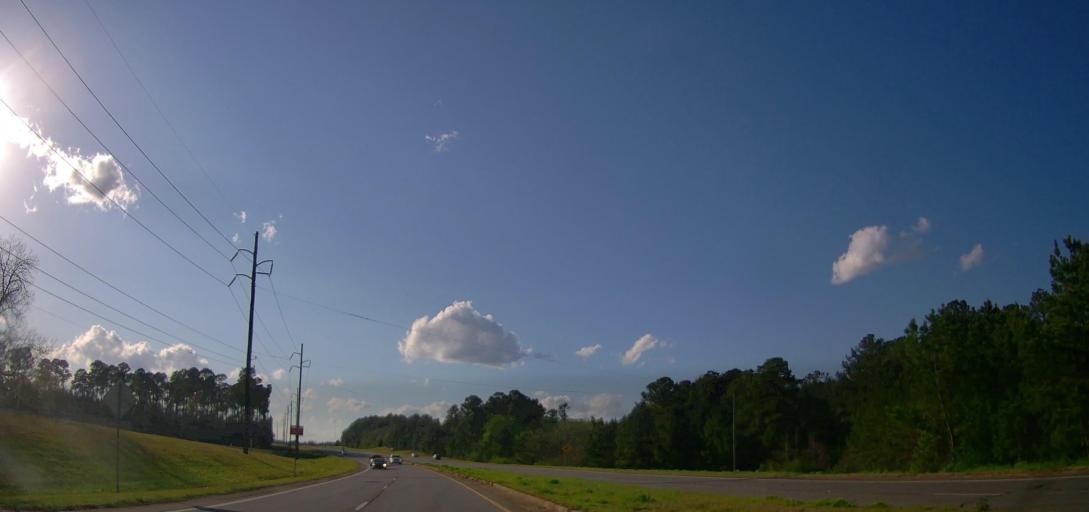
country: US
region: Georgia
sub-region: Baldwin County
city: Milledgeville
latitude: 33.0922
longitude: -83.2525
